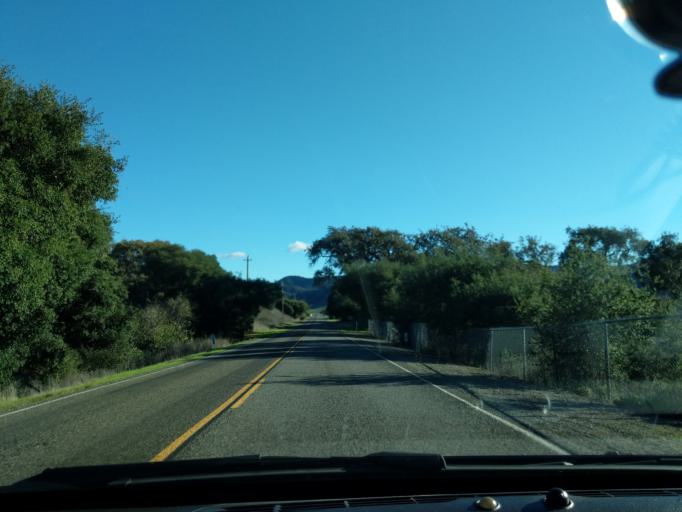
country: US
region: California
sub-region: Santa Barbara County
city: Los Alamos
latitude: 34.7533
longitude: -120.2939
